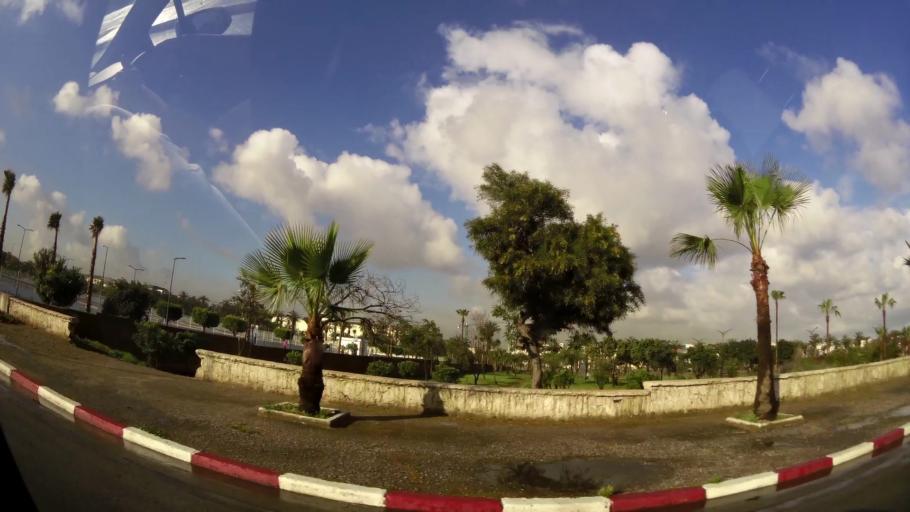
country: MA
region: Grand Casablanca
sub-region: Mediouna
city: Tit Mellil
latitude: 33.6021
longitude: -7.5278
